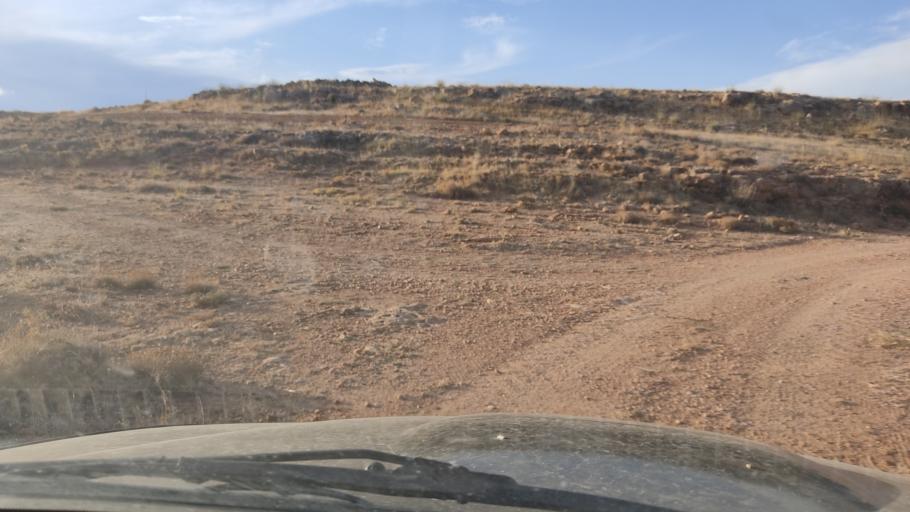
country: ES
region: Aragon
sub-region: Provincia de Teruel
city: Monforte de Moyuela
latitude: 41.0714
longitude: -0.9933
